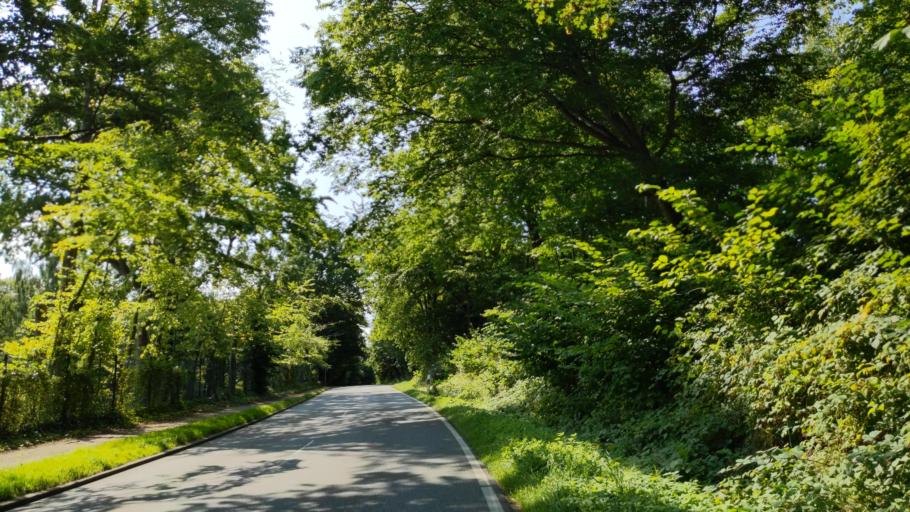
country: DE
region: Schleswig-Holstein
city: Malente
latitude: 54.1827
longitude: 10.5784
